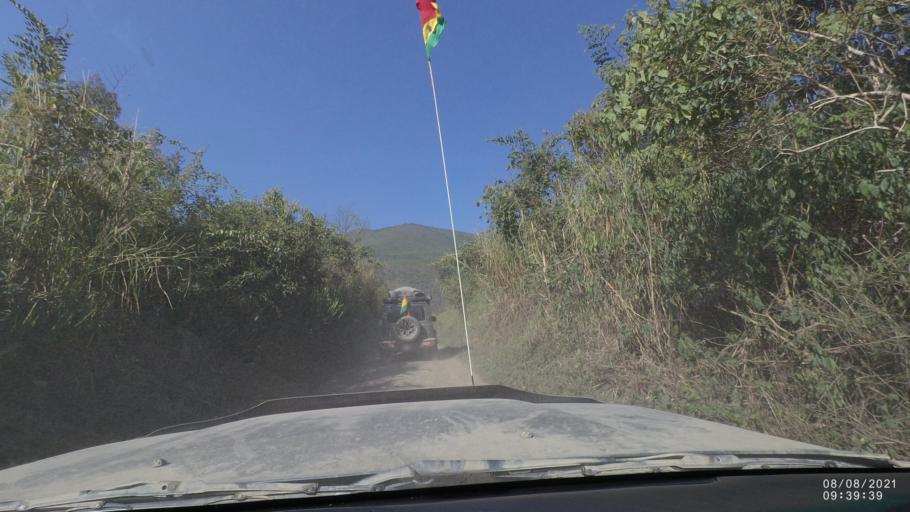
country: BO
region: La Paz
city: Quime
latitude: -16.5952
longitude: -66.7124
